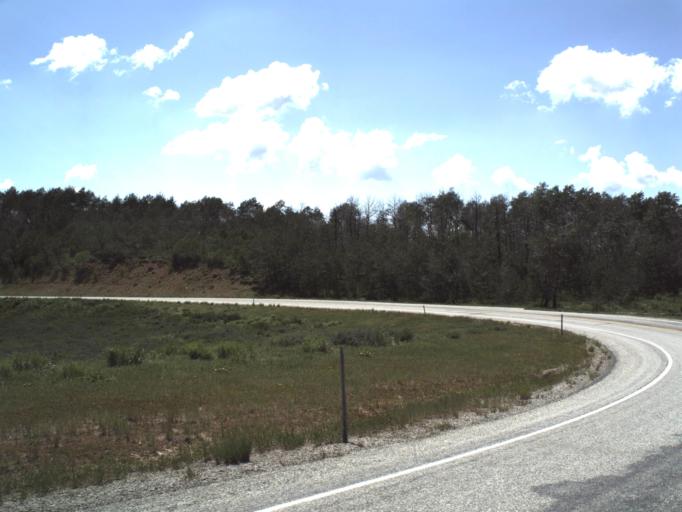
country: US
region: Utah
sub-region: Weber County
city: Wolf Creek
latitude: 41.4206
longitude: -111.5636
